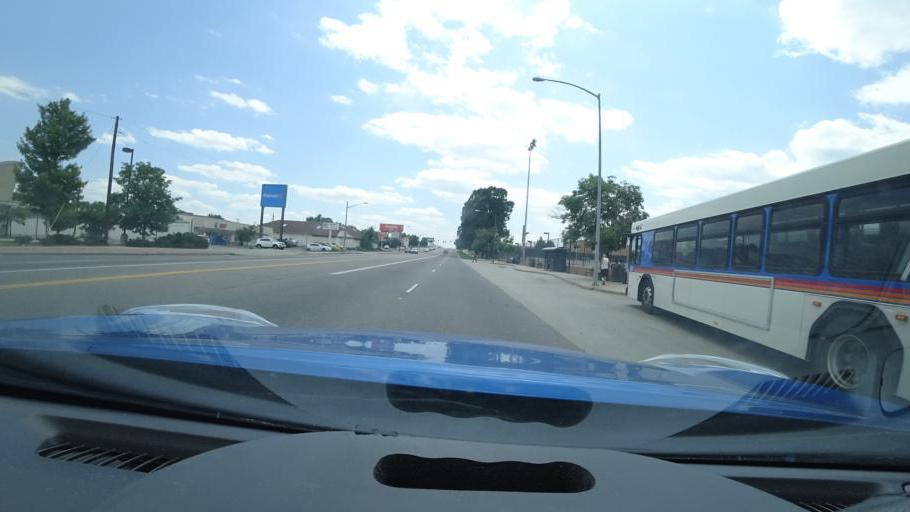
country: US
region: Colorado
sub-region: Arapahoe County
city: Sheridan
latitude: 39.6780
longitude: -105.0251
